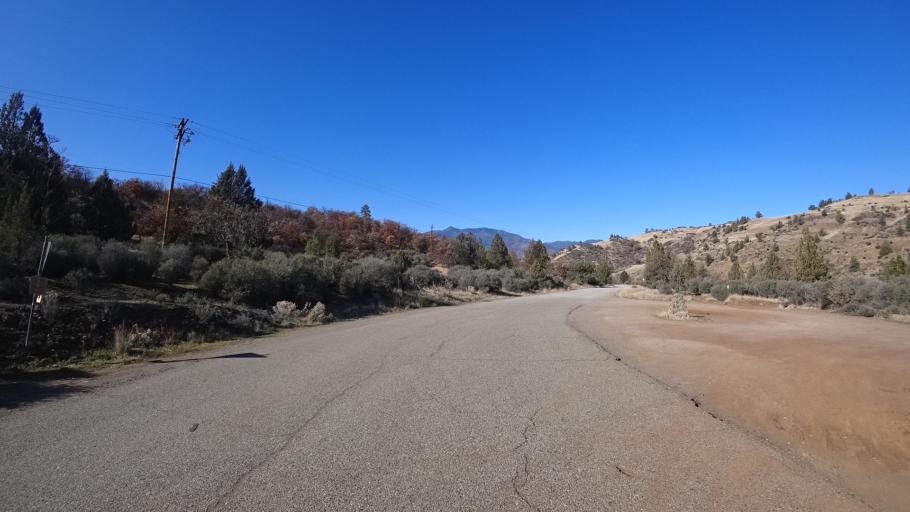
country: US
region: California
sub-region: Siskiyou County
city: Montague
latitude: 41.8983
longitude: -122.5092
